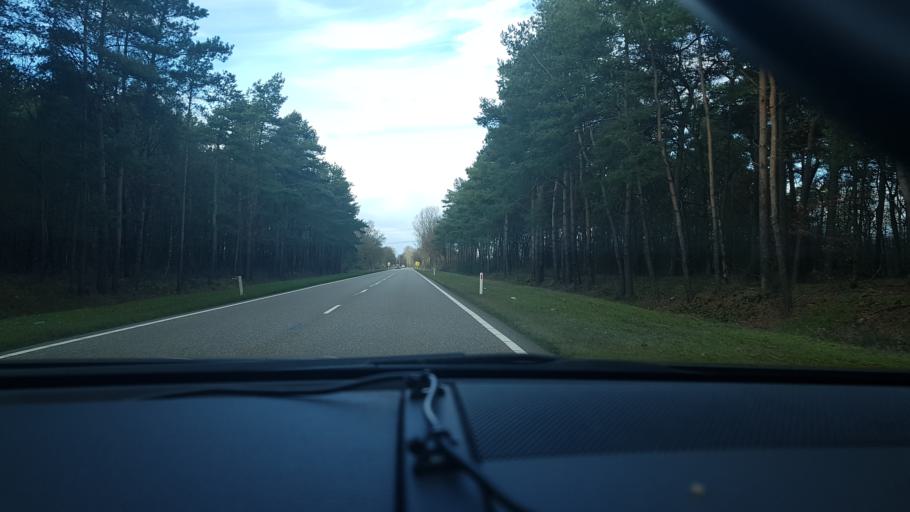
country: NL
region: Limburg
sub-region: Gemeente Peel en Maas
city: Maasbree
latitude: 51.3241
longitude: 6.0431
